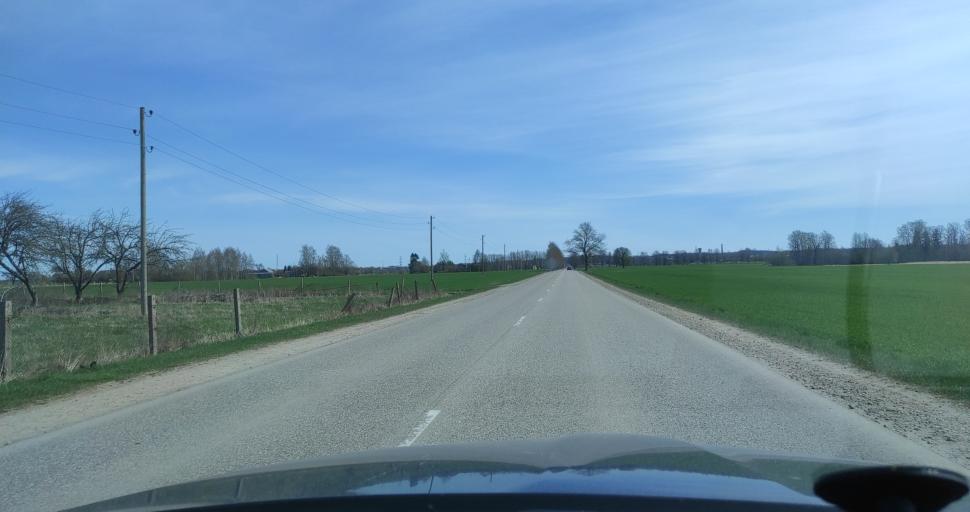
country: LV
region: Talsu Rajons
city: Talsi
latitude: 57.2285
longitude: 22.5337
